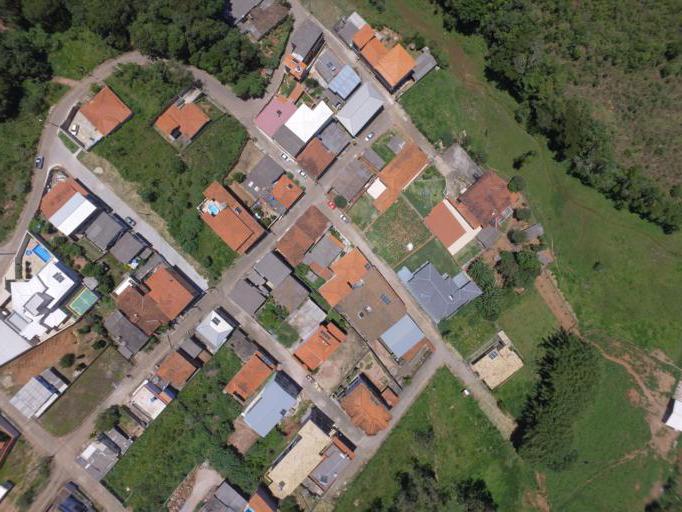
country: BR
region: Minas Gerais
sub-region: Tiradentes
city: Tiradentes
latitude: -21.0626
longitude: -44.0775
